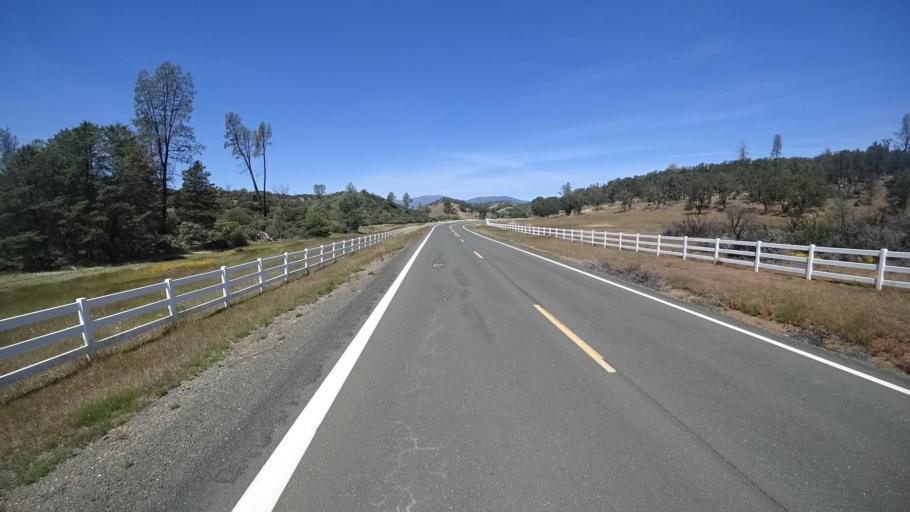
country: US
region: California
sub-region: Lake County
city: Hidden Valley Lake
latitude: 38.7234
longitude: -122.5100
